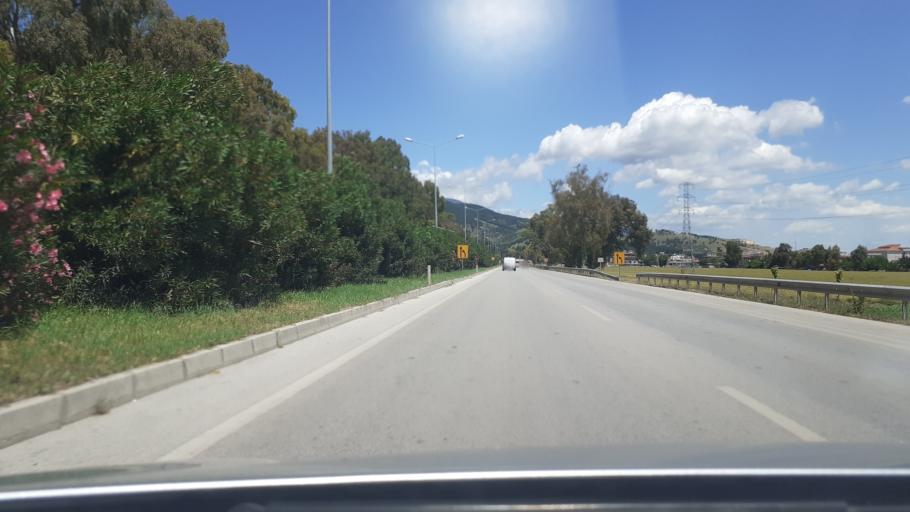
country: TR
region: Hatay
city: Serinyol
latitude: 36.3807
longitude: 36.2290
